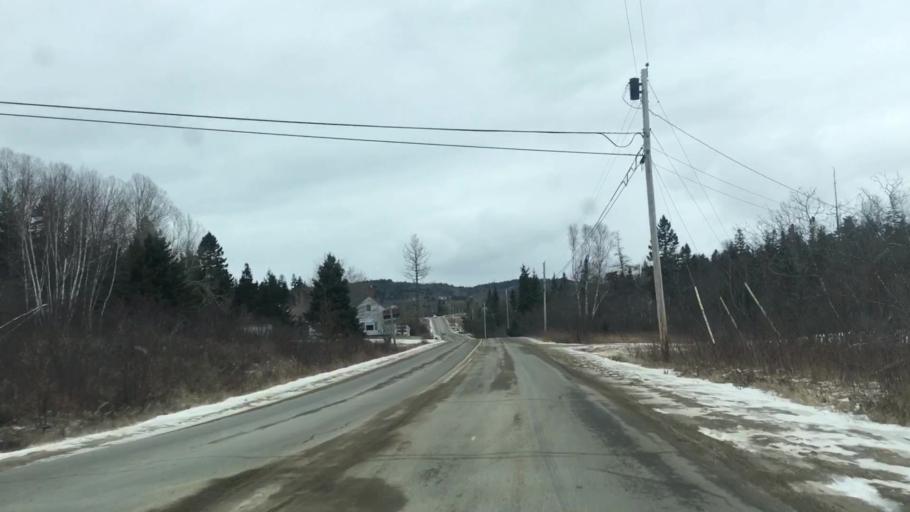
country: US
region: Maine
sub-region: Washington County
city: Machiasport
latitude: 44.7066
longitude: -67.4027
